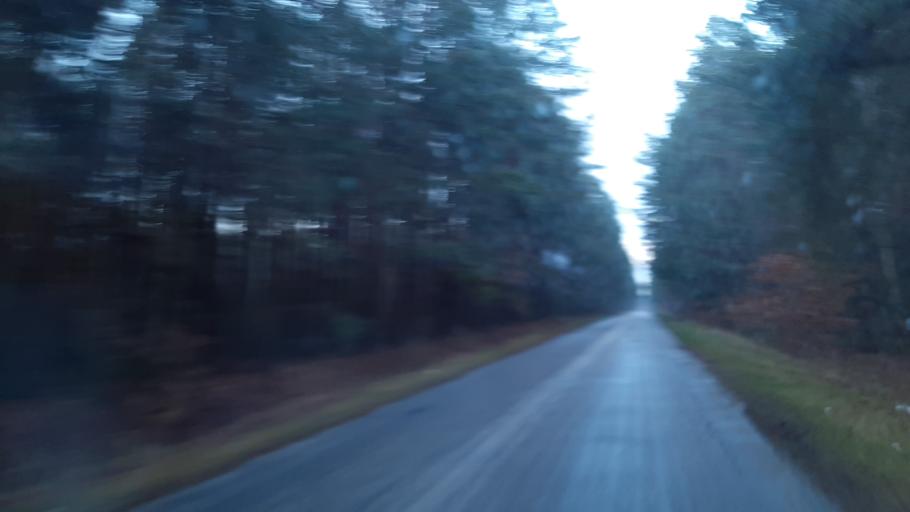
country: PL
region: Lublin Voivodeship
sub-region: Powiat lubartowski
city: Kamionka
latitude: 51.4827
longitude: 22.4735
